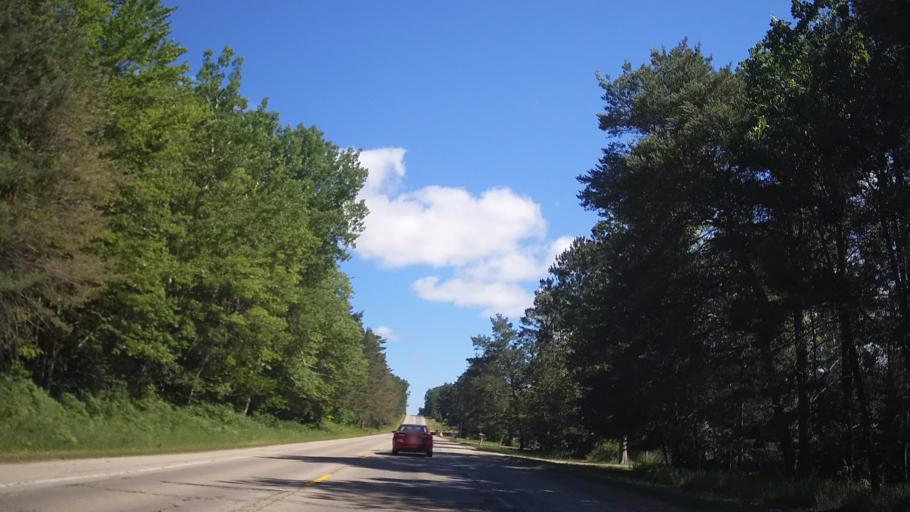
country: US
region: Michigan
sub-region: Cheboygan County
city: Indian River
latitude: 45.4527
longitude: -84.7843
